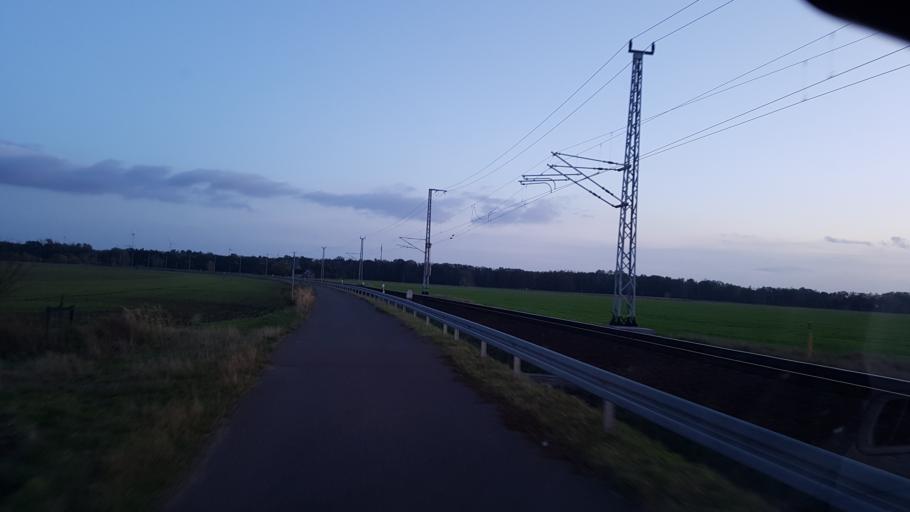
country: DE
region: Brandenburg
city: Doberlug-Kirchhain
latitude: 51.6402
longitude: 13.5778
